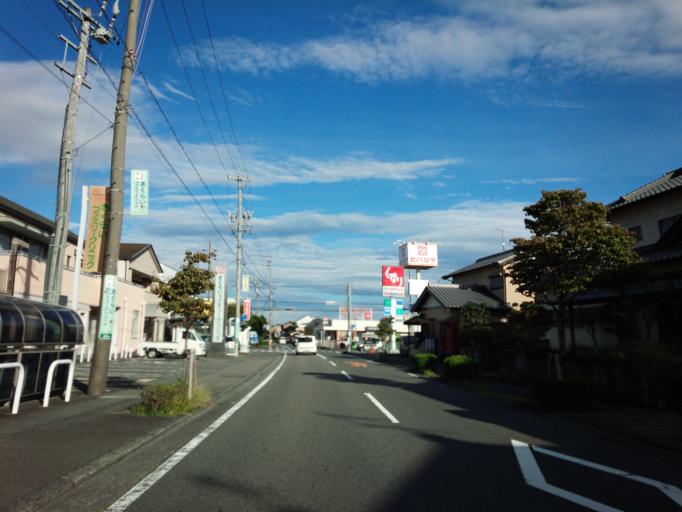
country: JP
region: Shizuoka
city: Kanaya
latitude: 34.8417
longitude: 138.1558
